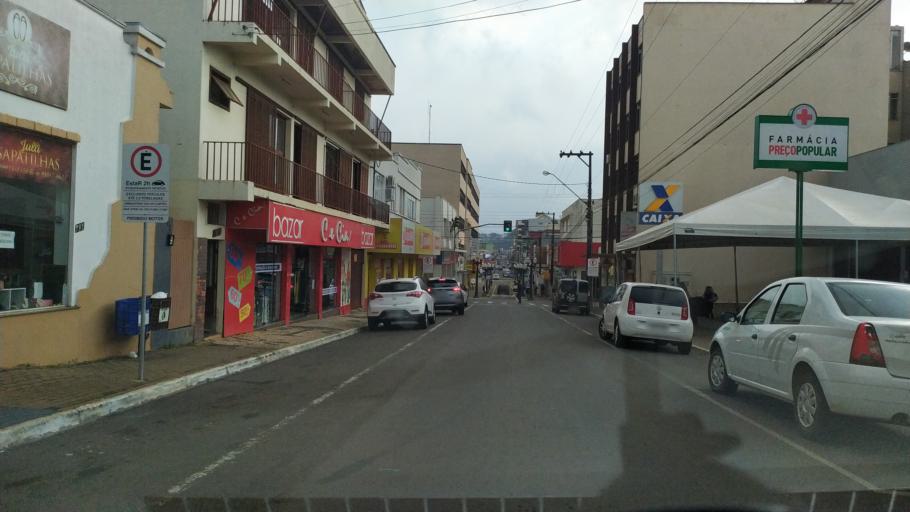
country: BR
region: Parana
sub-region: Palmas
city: Palmas
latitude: -26.4836
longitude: -51.9898
